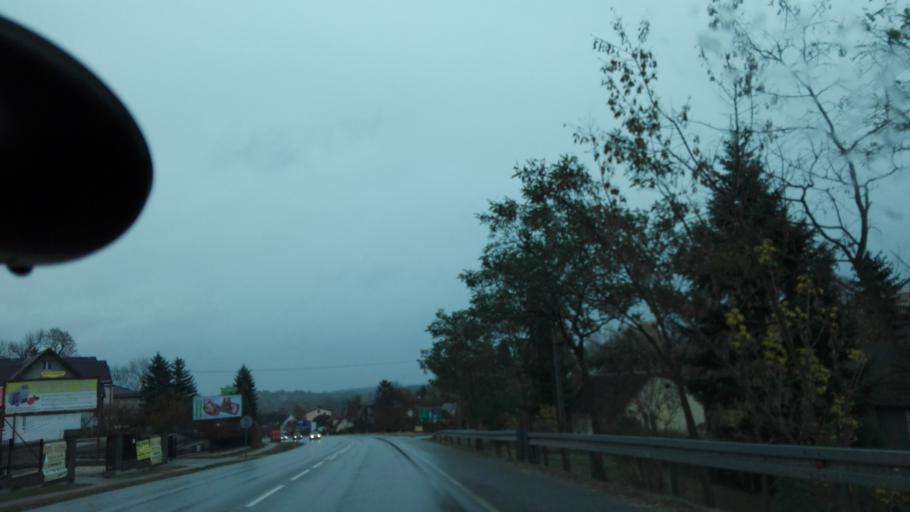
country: PL
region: Lublin Voivodeship
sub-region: Powiat pulawski
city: Pulawy
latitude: 51.4097
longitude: 21.9289
